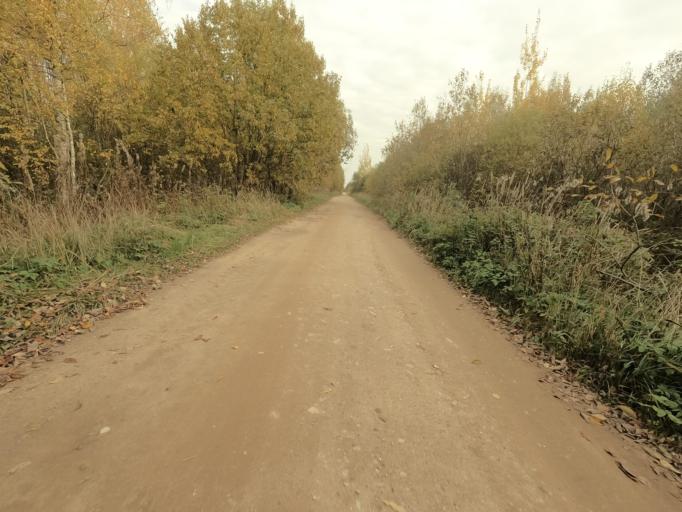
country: RU
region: Novgorod
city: Pankovka
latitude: 58.8972
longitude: 30.9997
